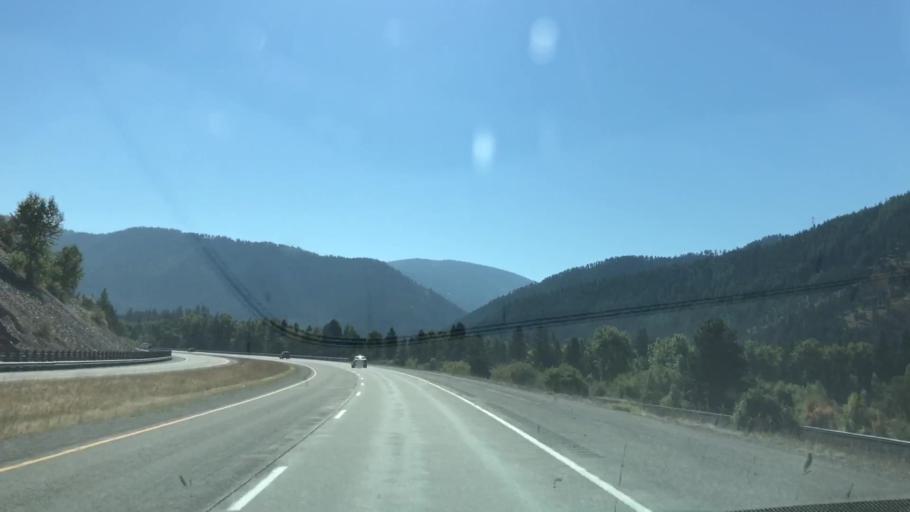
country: US
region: Montana
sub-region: Missoula County
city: Clinton
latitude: 46.7289
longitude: -113.6948
